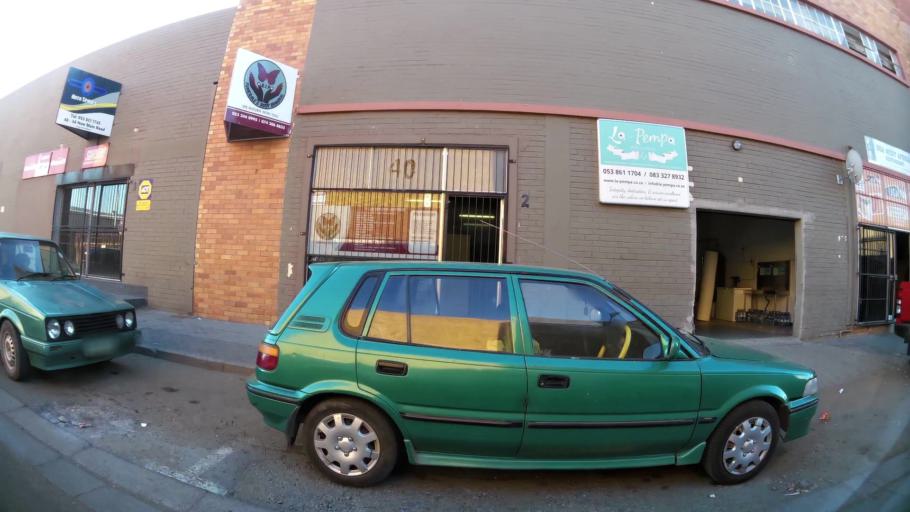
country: ZA
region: Northern Cape
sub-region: Frances Baard District Municipality
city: Kimberley
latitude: -28.7411
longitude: 24.7607
